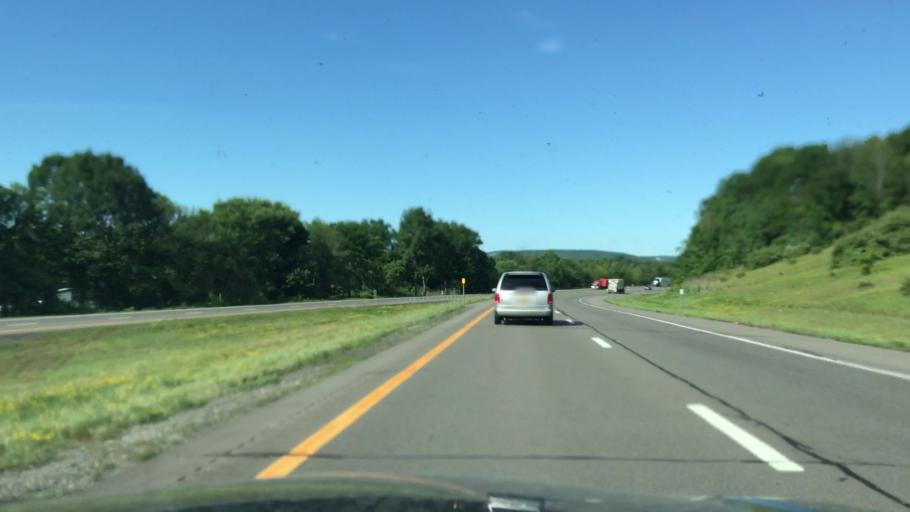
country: US
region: New York
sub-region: Tioga County
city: Owego
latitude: 42.0803
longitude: -76.3053
